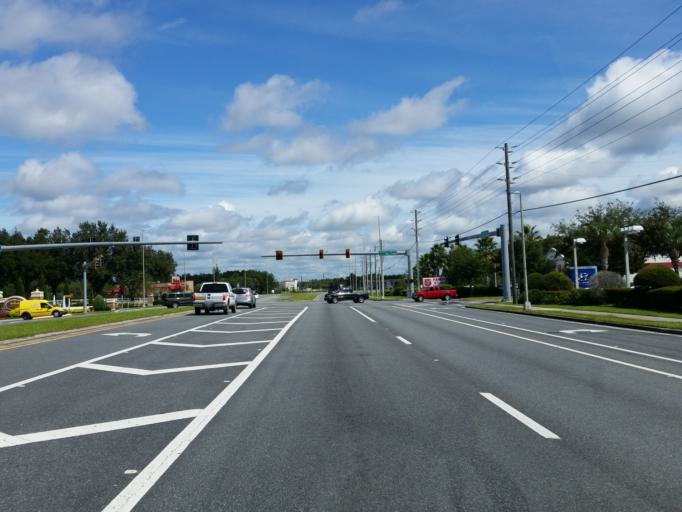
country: US
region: Florida
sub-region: Pasco County
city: Wesley Chapel
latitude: 28.2345
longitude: -82.3699
